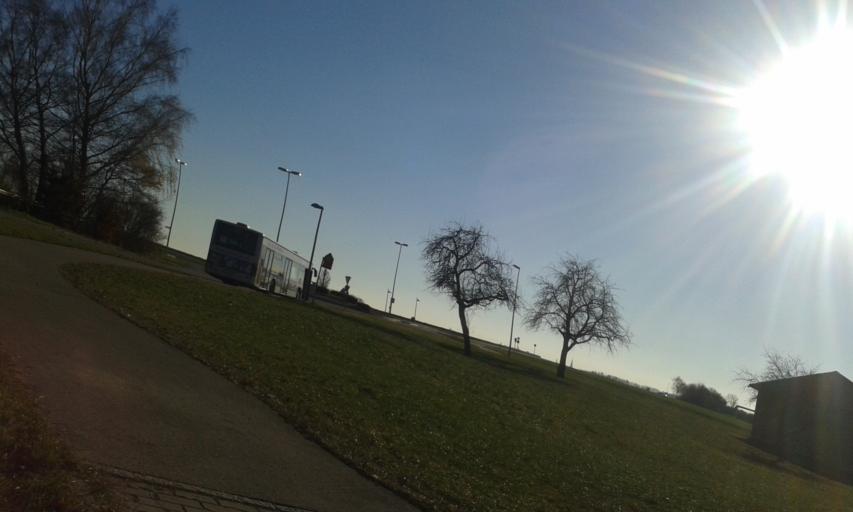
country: DE
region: Baden-Wuerttemberg
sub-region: Tuebingen Region
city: Ulm
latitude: 48.4399
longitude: 9.9863
